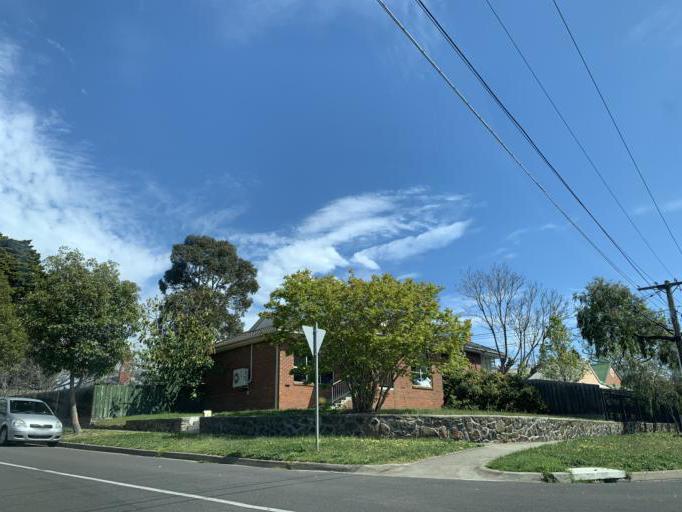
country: AU
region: Victoria
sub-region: Bayside
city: Hampton East
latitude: -37.9410
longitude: 145.0280
